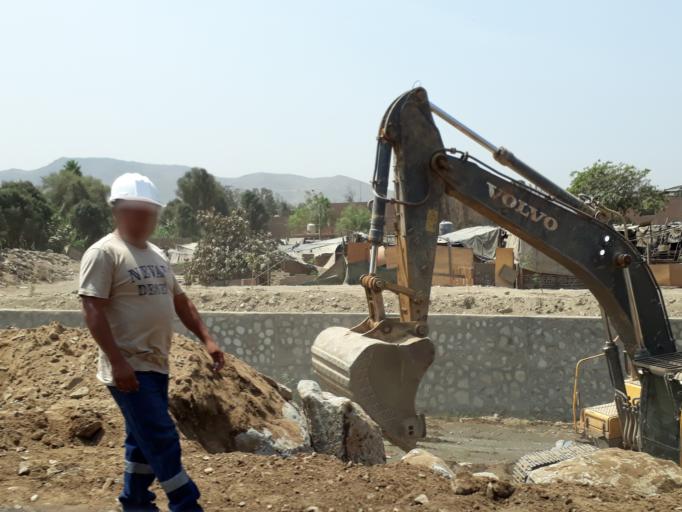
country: PE
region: Lima
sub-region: Lima
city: Santa Maria
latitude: -11.9945
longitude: -76.9096
